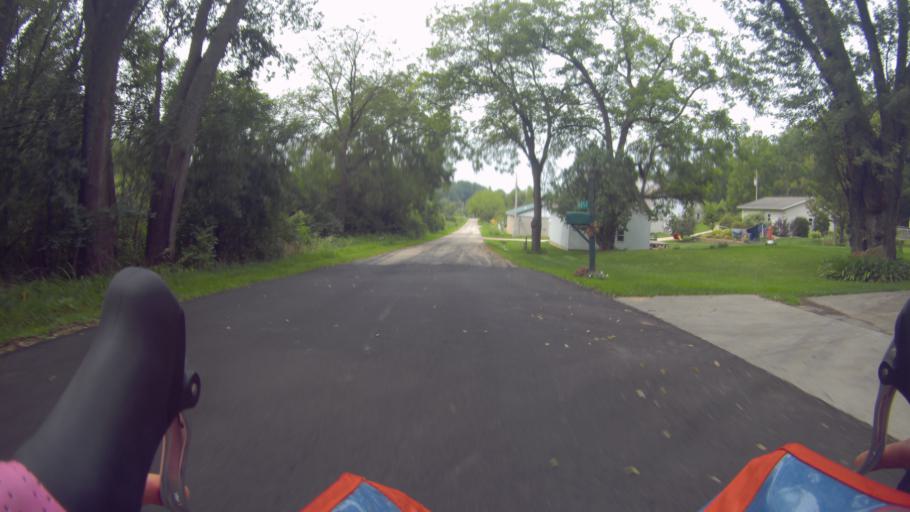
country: US
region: Wisconsin
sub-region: Dane County
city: Mount Horeb
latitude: 42.9847
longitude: -89.6731
